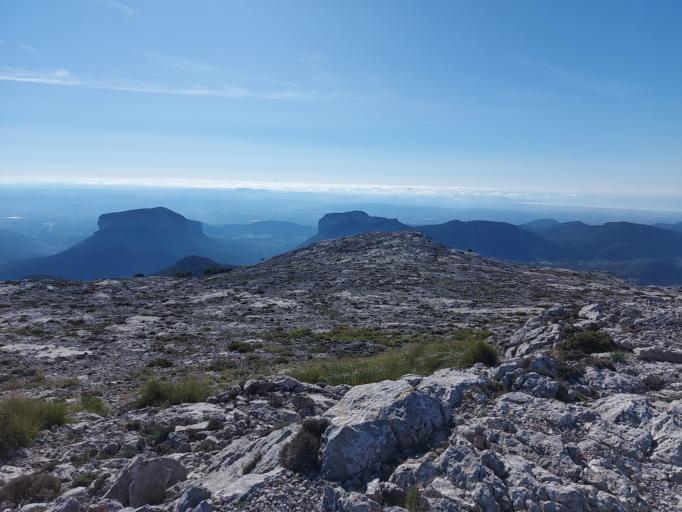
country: ES
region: Balearic Islands
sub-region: Illes Balears
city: Fornalutx
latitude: 39.7741
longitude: 2.7829
